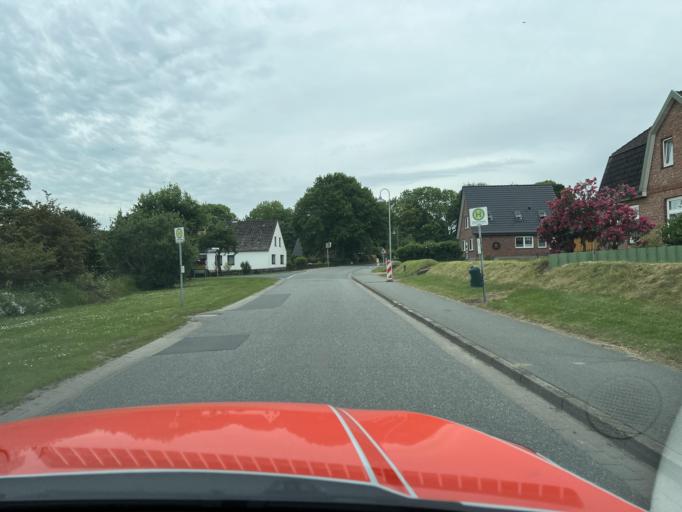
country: DE
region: Schleswig-Holstein
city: Hemmingstedt
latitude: 54.1585
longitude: 9.0923
